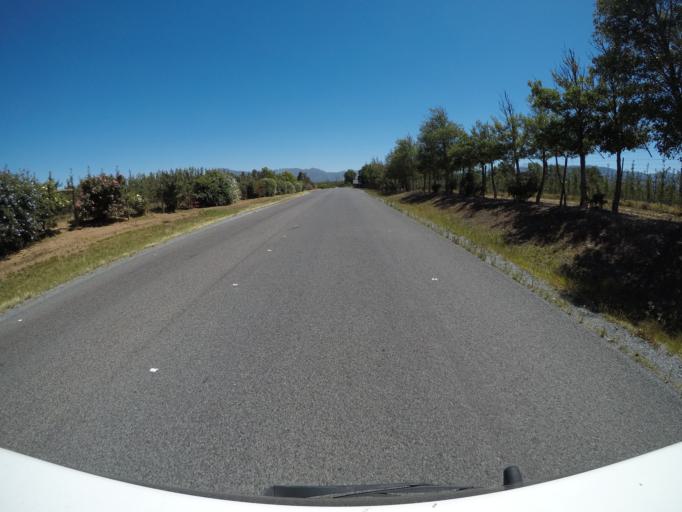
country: ZA
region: Western Cape
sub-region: Overberg District Municipality
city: Grabouw
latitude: -34.1900
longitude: 19.0401
